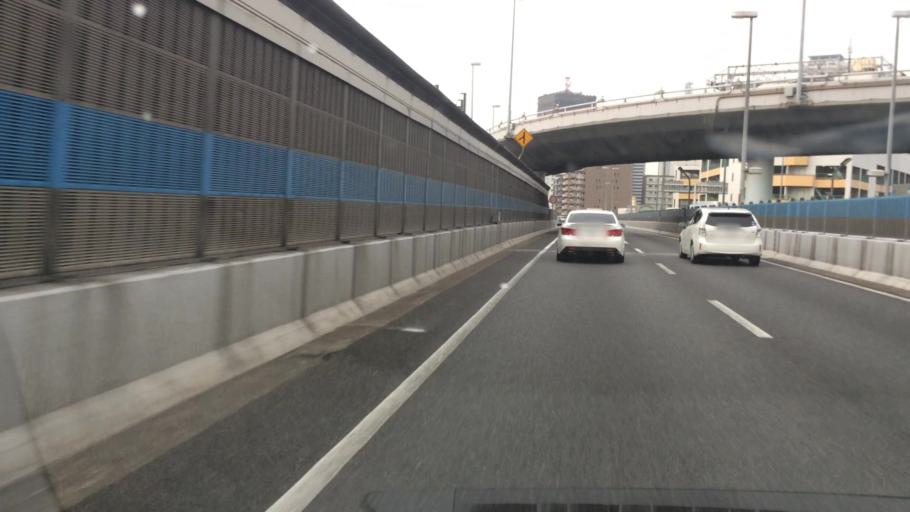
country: JP
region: Hyogo
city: Kobe
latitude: 34.6937
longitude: 135.2041
